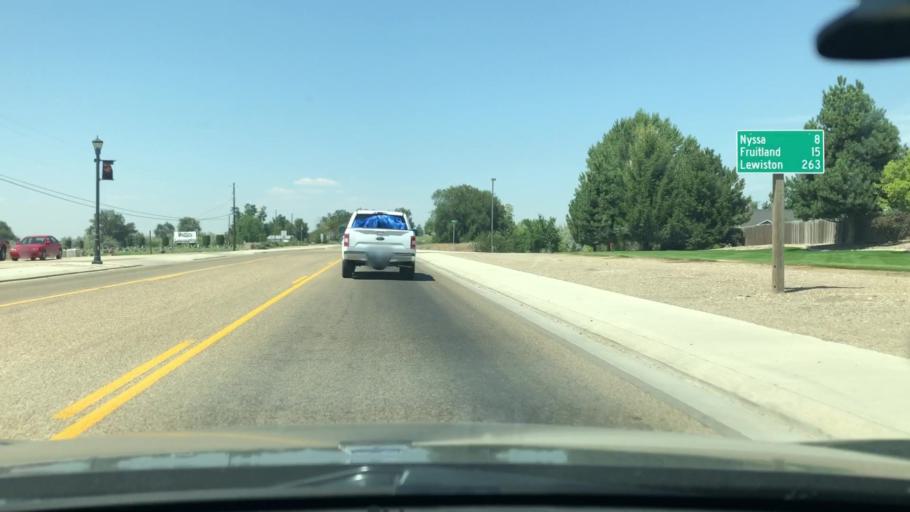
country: US
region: Idaho
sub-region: Canyon County
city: Parma
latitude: 43.7904
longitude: -116.9495
